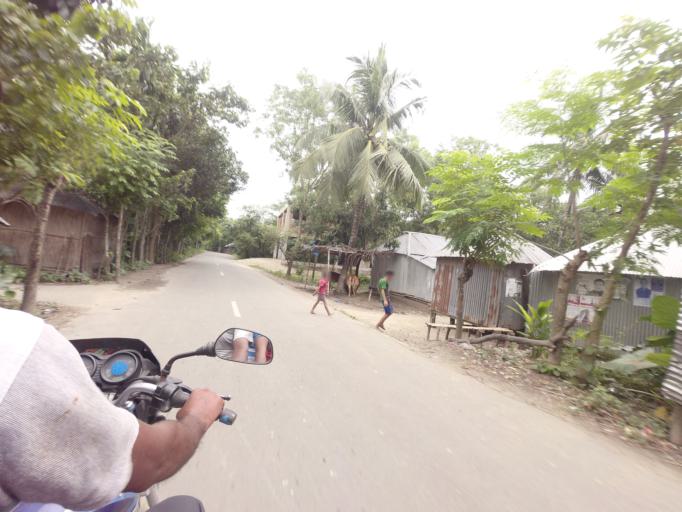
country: BD
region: Khulna
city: Kalia
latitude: 23.1541
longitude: 89.6447
